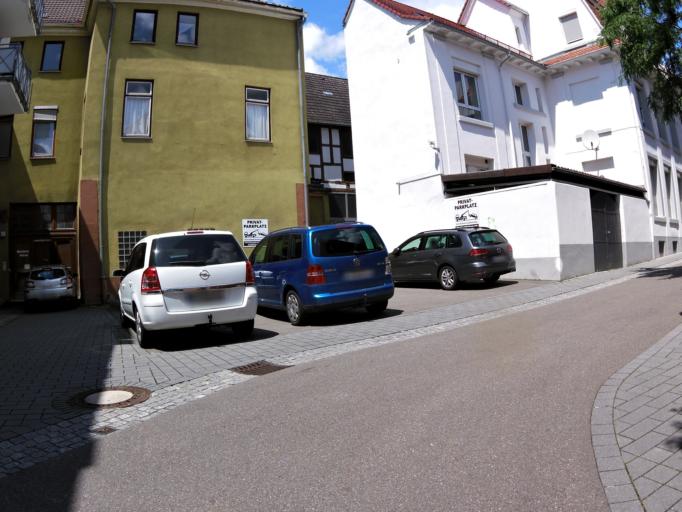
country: DE
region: Baden-Wuerttemberg
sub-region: Freiburg Region
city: Lahr
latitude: 48.3414
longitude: 7.8736
